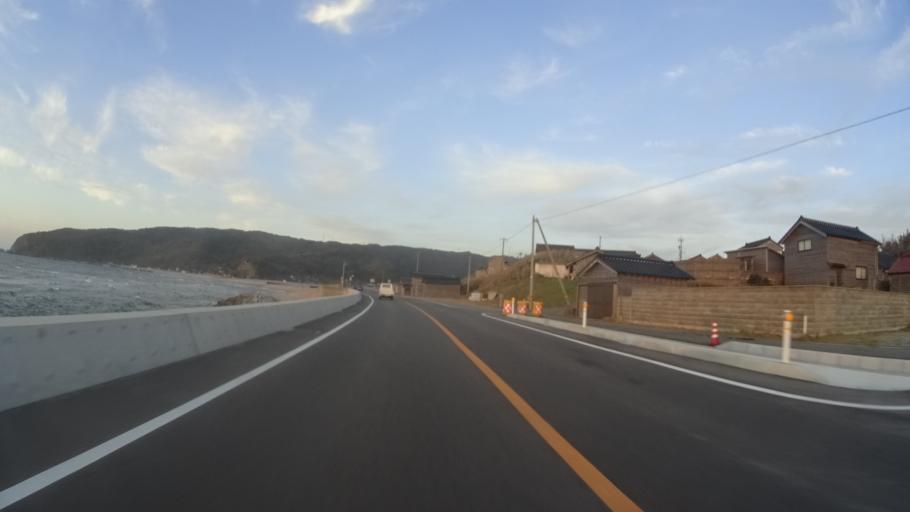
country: JP
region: Ishikawa
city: Nanao
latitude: 37.2833
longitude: 136.7348
